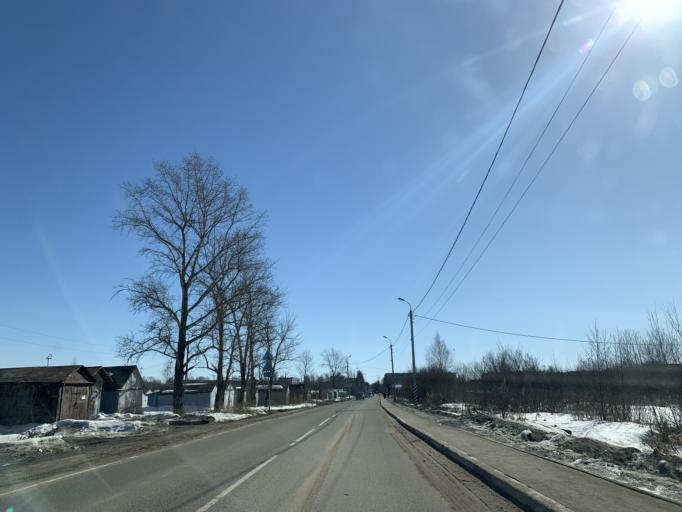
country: RU
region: Jaroslavl
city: Konstantinovskiy
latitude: 57.8359
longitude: 39.5876
